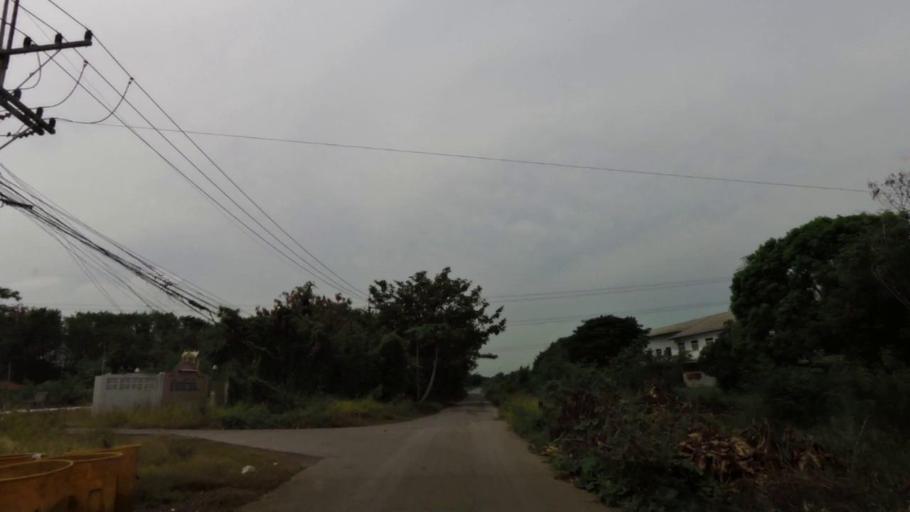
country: TH
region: Lop Buri
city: Ban Mi
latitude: 15.0458
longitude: 100.5602
